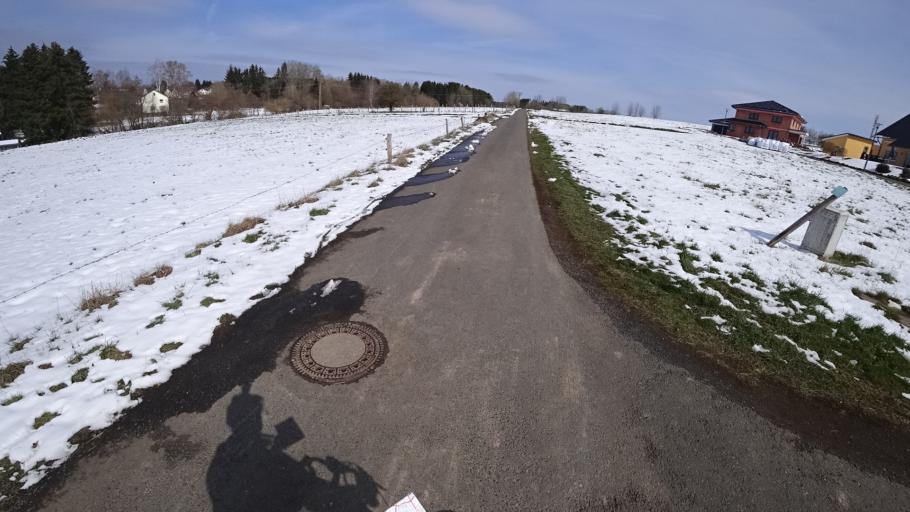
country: DE
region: Rheinland-Pfalz
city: Morlen
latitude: 50.6991
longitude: 7.8836
